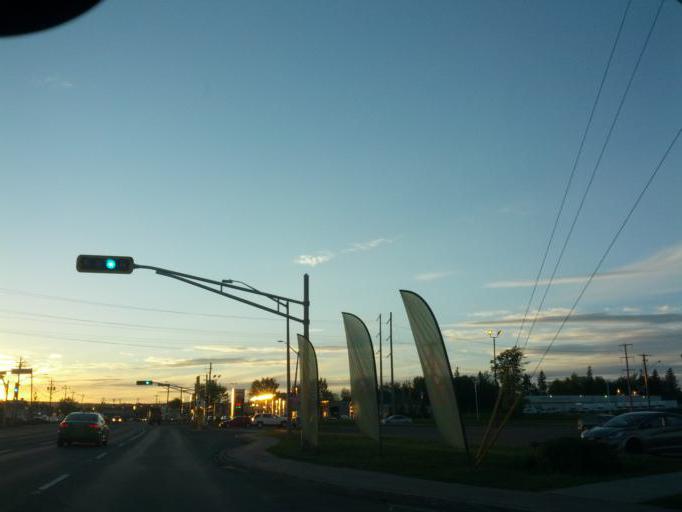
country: CA
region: New Brunswick
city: Moncton
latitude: 46.1134
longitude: -64.8359
